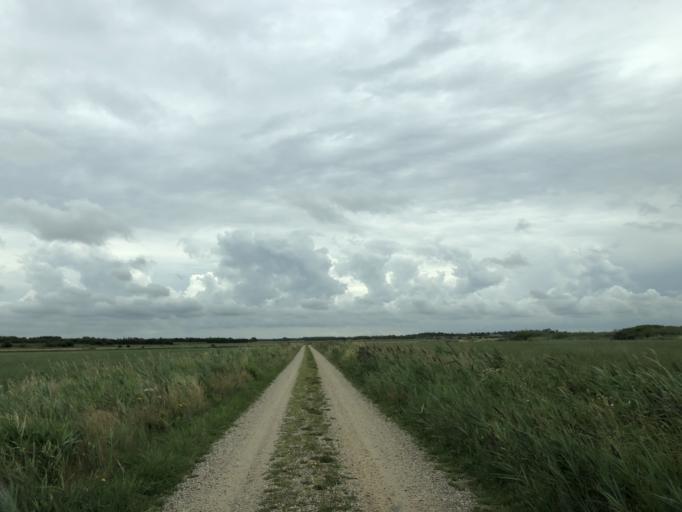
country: DK
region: Central Jutland
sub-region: Ringkobing-Skjern Kommune
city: Ringkobing
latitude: 56.1270
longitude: 8.2464
